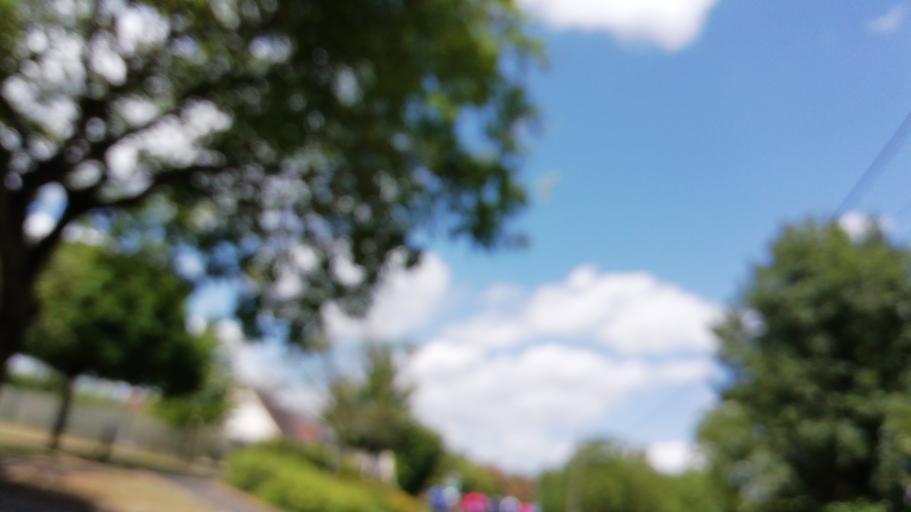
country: FR
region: Poitou-Charentes
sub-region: Departement de la Vienne
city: Thure
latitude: 46.8338
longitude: 0.4572
